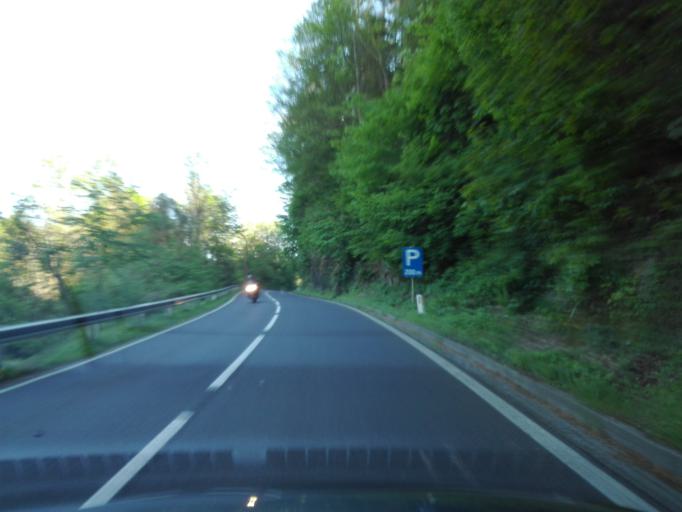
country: AT
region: Upper Austria
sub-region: Politischer Bezirk Rohrbach
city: Pfarrkirchen im Muehlkreis
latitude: 48.4669
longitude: 13.7799
